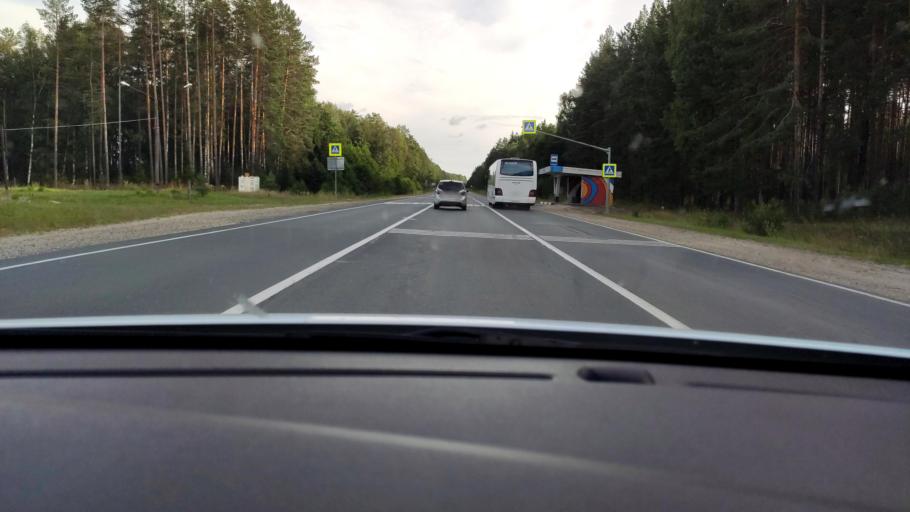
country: RU
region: Mariy-El
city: Suslonger
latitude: 56.3107
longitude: 48.2347
